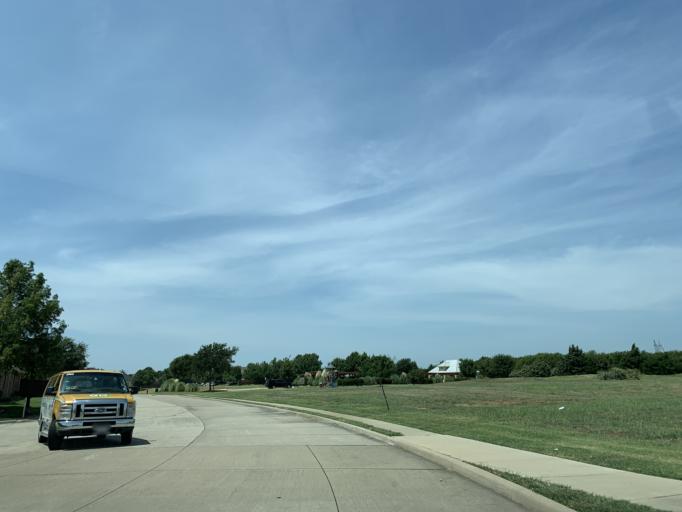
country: US
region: Texas
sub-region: Dallas County
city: Cedar Hill
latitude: 32.6460
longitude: -97.0420
